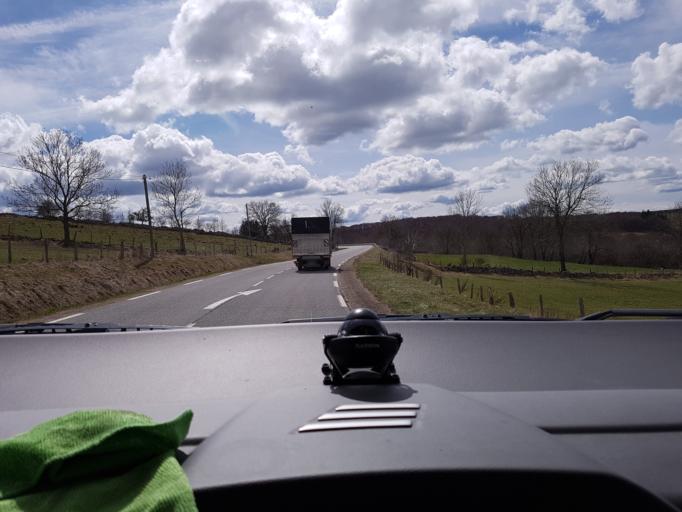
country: FR
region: Midi-Pyrenees
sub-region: Departement de l'Aveyron
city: Laguiole
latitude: 44.7519
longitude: 2.8723
